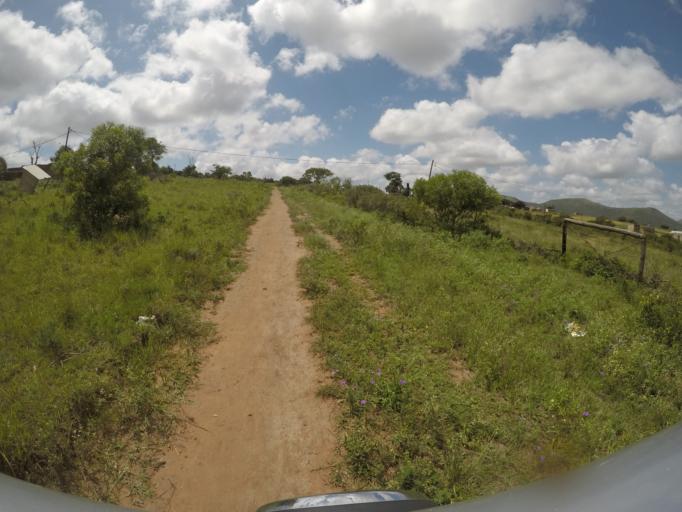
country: ZA
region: KwaZulu-Natal
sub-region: uThungulu District Municipality
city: Empangeni
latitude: -28.5823
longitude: 31.8406
